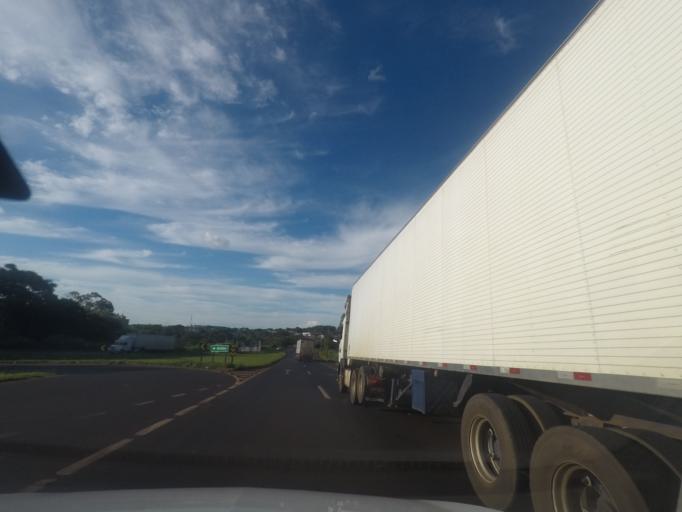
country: BR
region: Goias
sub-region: Itumbiara
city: Itumbiara
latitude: -18.4212
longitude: -49.1945
